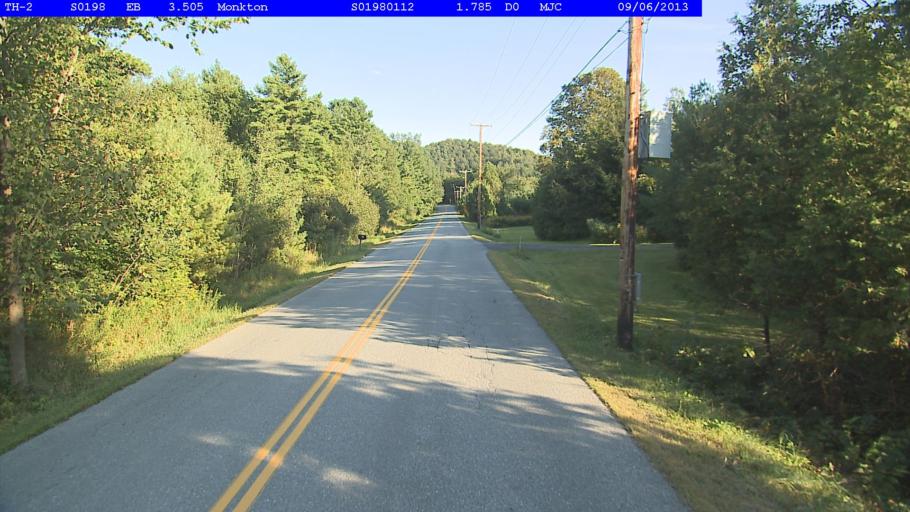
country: US
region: Vermont
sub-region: Chittenden County
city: Hinesburg
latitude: 44.2448
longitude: -73.1652
